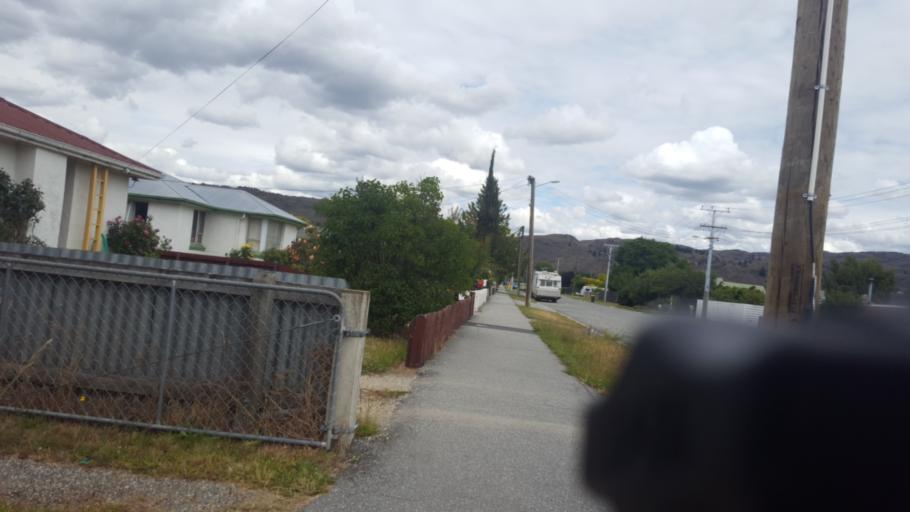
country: NZ
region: Otago
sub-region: Queenstown-Lakes District
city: Wanaka
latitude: -45.2508
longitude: 169.3856
